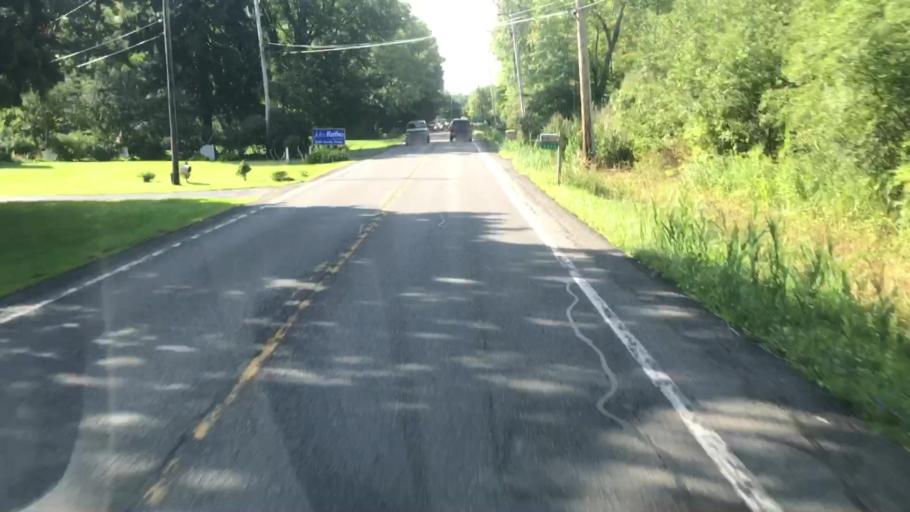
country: US
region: New York
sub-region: Onondaga County
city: Skaneateles
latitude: 42.9569
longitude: -76.4259
